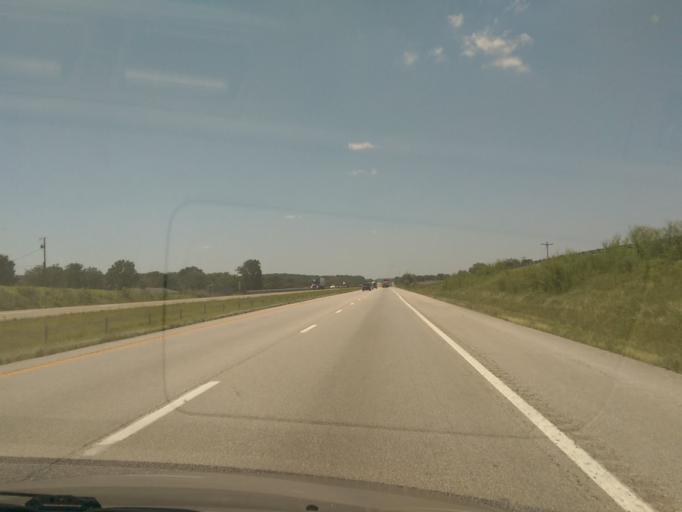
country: US
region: Missouri
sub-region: Cooper County
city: Boonville
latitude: 38.9353
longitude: -92.8608
